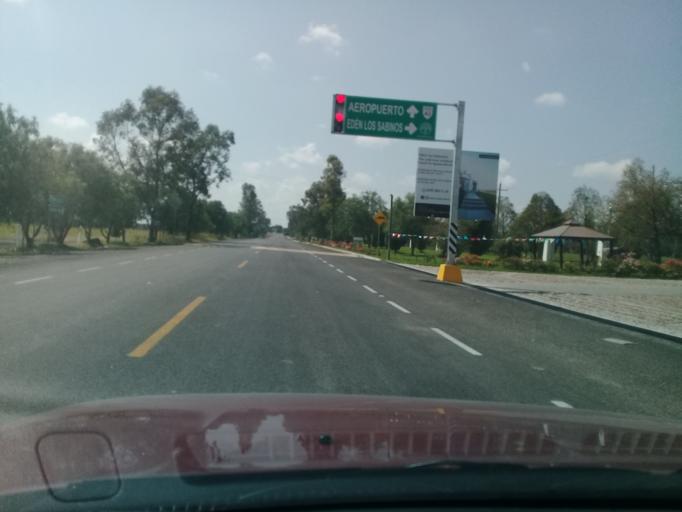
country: MX
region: Aguascalientes
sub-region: Aguascalientes
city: Penuelas (El Cienegal)
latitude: 21.7278
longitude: -102.3605
